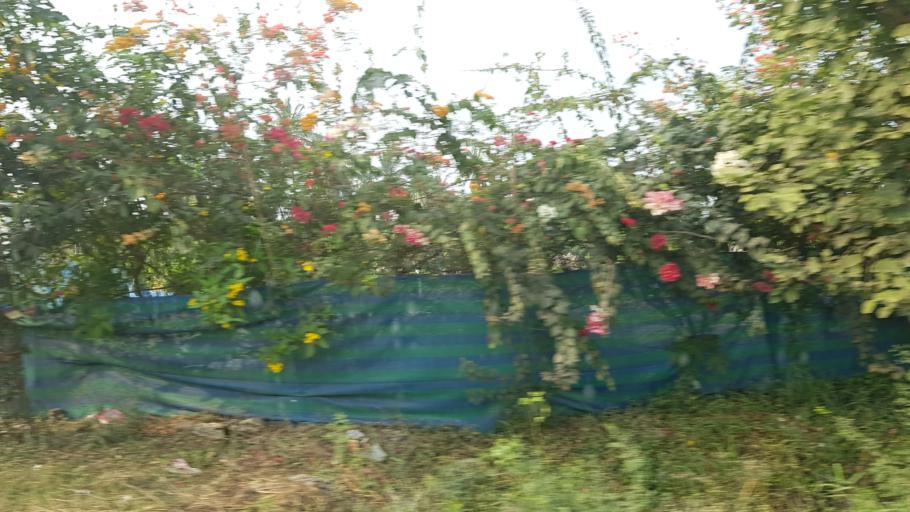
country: IN
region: Andhra Pradesh
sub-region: West Godavari
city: Akividu
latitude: 16.5210
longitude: 81.3755
